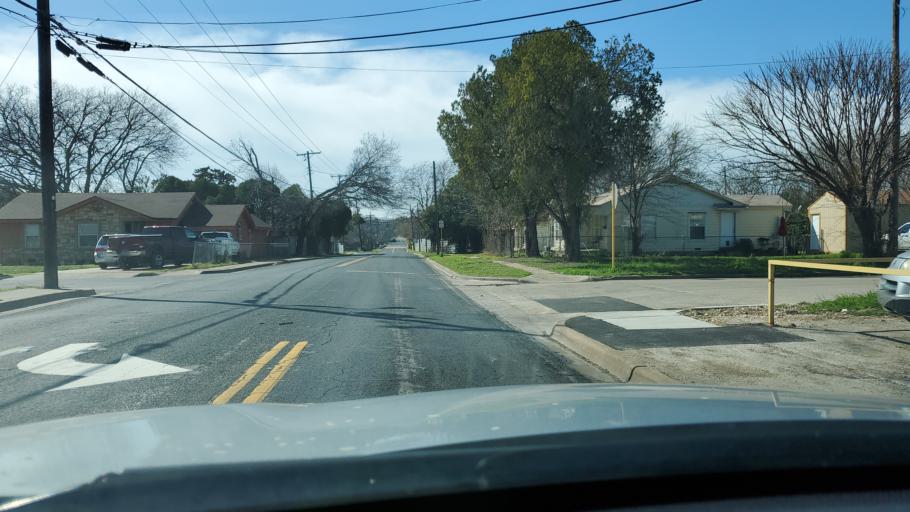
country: US
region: Texas
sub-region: Bell County
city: Killeen
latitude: 31.1159
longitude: -97.7269
